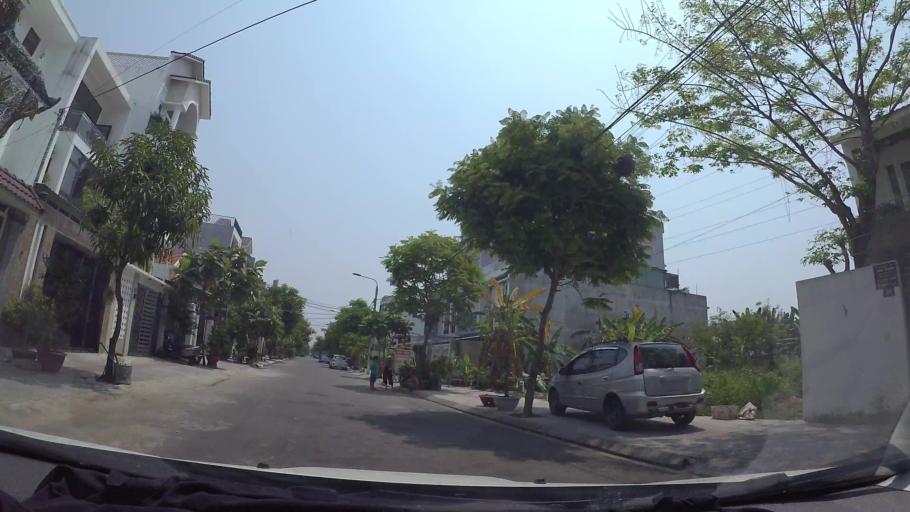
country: VN
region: Da Nang
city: Cam Le
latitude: 16.0217
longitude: 108.2241
